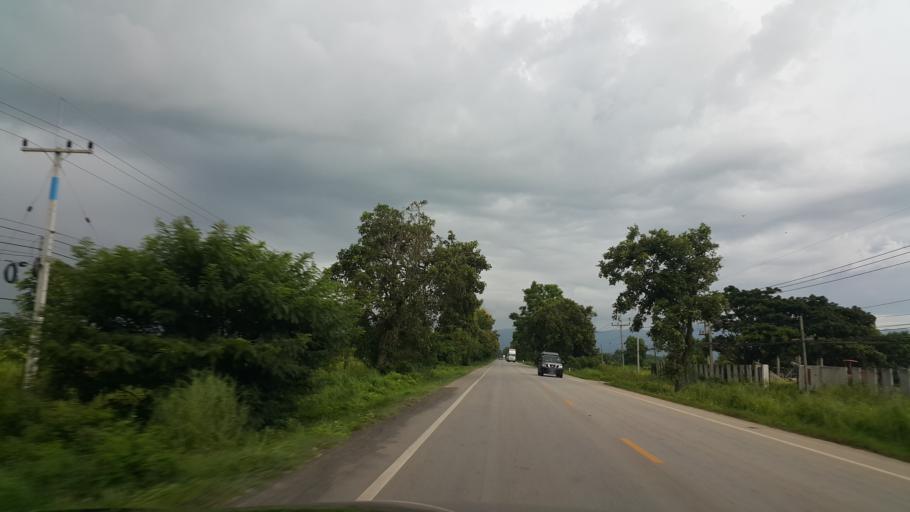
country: TH
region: Phayao
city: Dok Kham Tai
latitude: 19.1838
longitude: 100.0167
